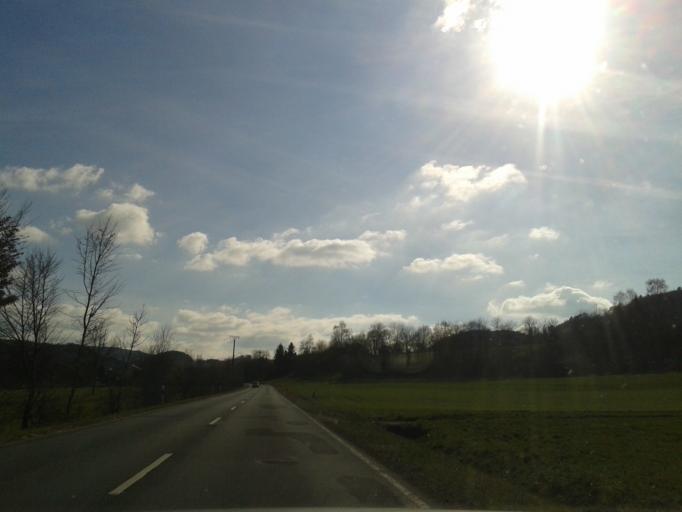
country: DE
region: Hesse
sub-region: Regierungsbezirk Giessen
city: Breidenbach
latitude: 50.8315
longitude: 8.4557
